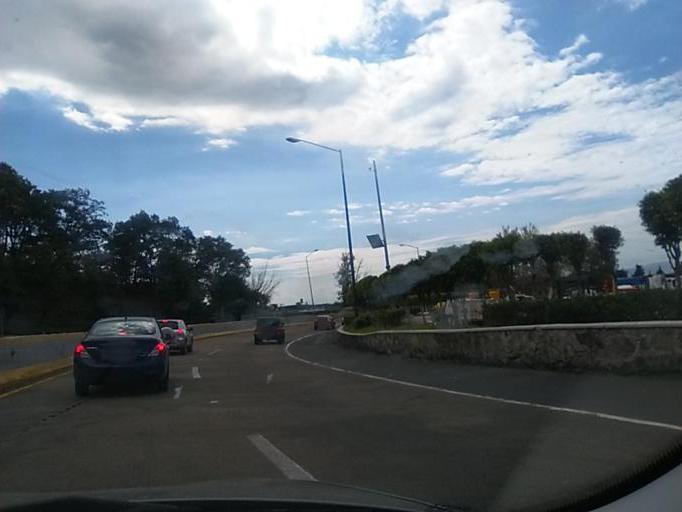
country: MX
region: Morelos
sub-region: Tepoztlan
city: Santa Catarina
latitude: 19.0213
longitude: -99.1369
